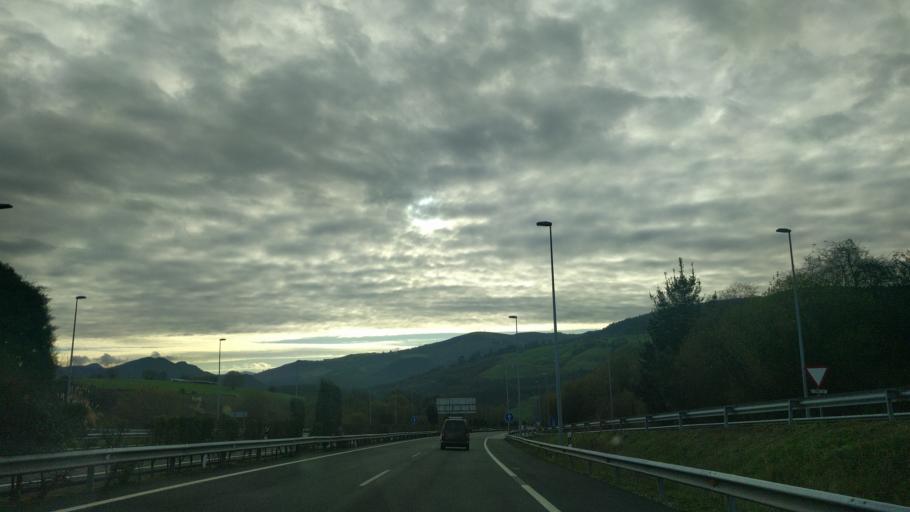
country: ES
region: Cantabria
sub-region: Provincia de Cantabria
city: Laredo
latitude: 43.3981
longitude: -3.4000
